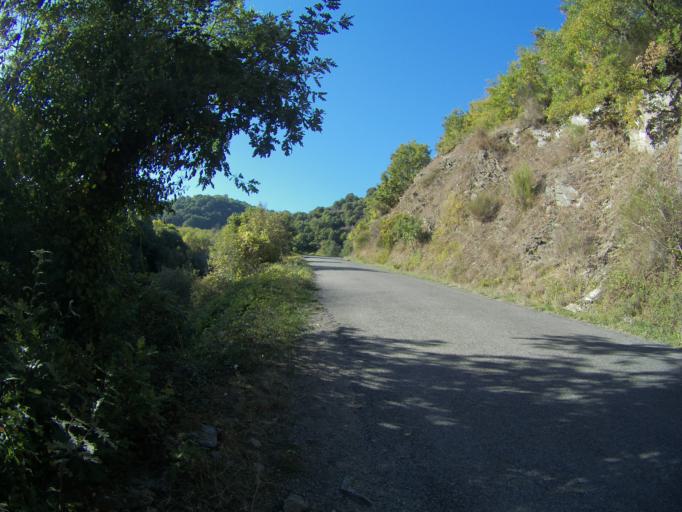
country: ES
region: Castille and Leon
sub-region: Provincia de Leon
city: Vega de Valcarce
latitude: 42.6748
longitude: -6.9947
